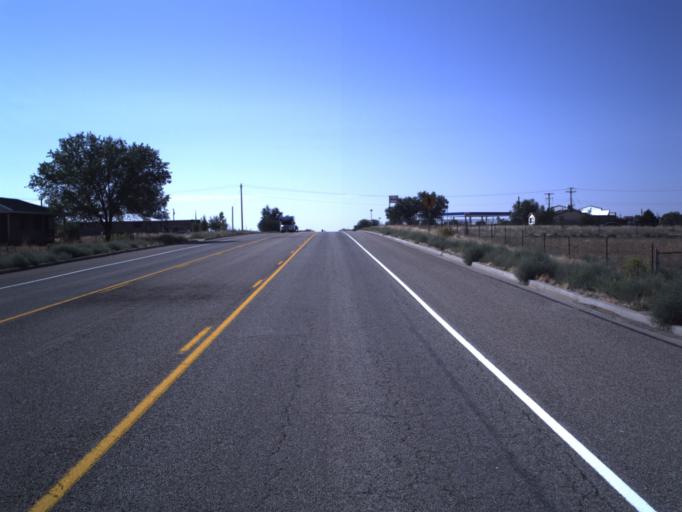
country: US
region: Utah
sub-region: San Juan County
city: Blanding
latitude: 37.4678
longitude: -109.4670
